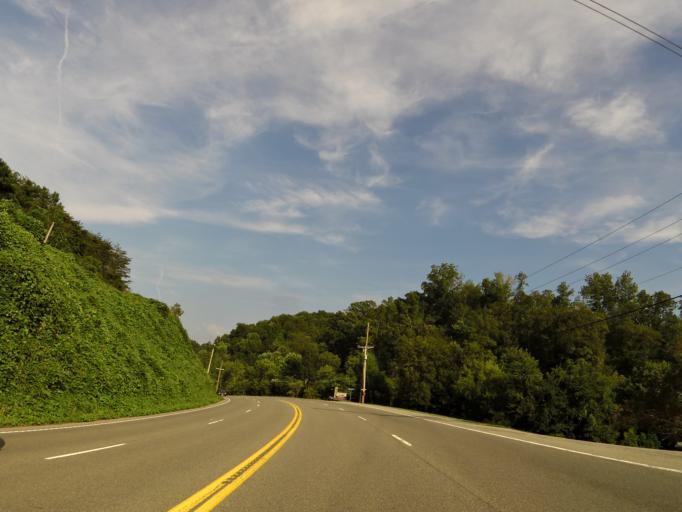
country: US
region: Tennessee
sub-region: Sevier County
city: Seymour
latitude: 35.8583
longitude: -83.6515
